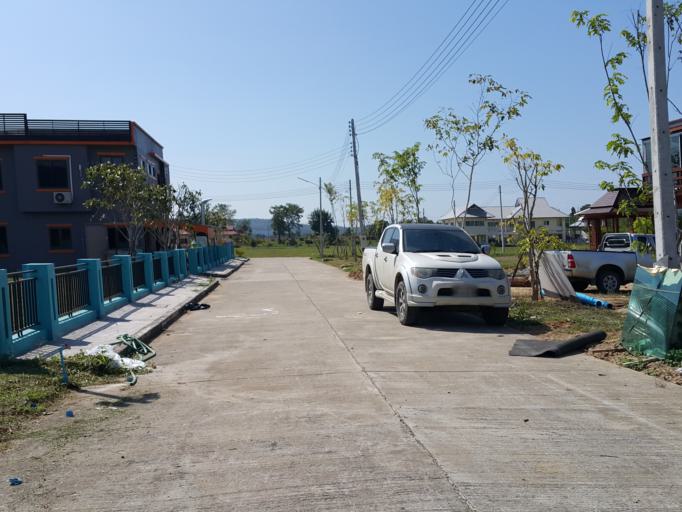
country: TH
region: Chiang Mai
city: San Sai
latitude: 18.8808
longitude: 99.1653
